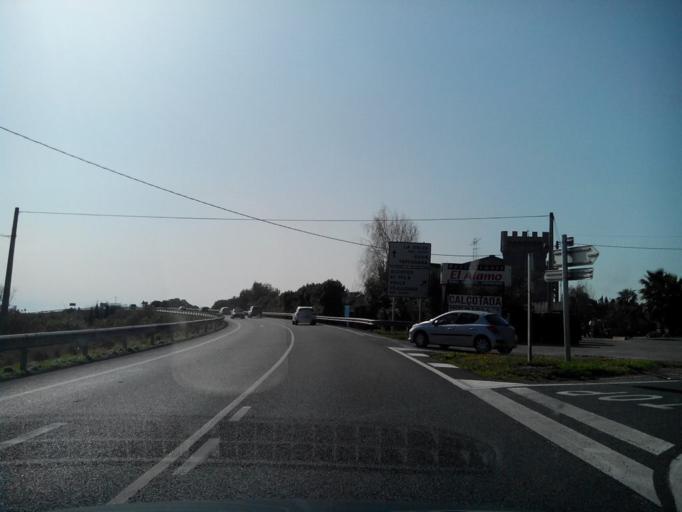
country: ES
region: Catalonia
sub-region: Provincia de Tarragona
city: Alcover
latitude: 41.2689
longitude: 1.1748
